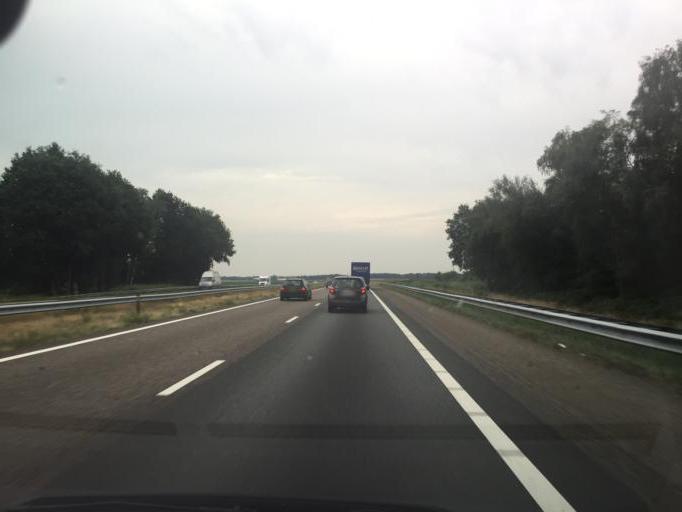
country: NL
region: North Brabant
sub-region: Gemeente Asten
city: Asten
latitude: 51.3864
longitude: 5.8815
